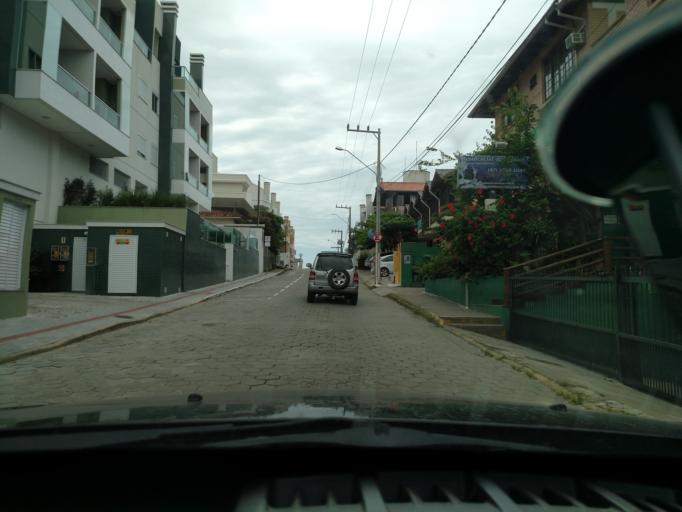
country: BR
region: Santa Catarina
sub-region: Porto Belo
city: Porto Belo
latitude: -27.1505
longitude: -48.4851
